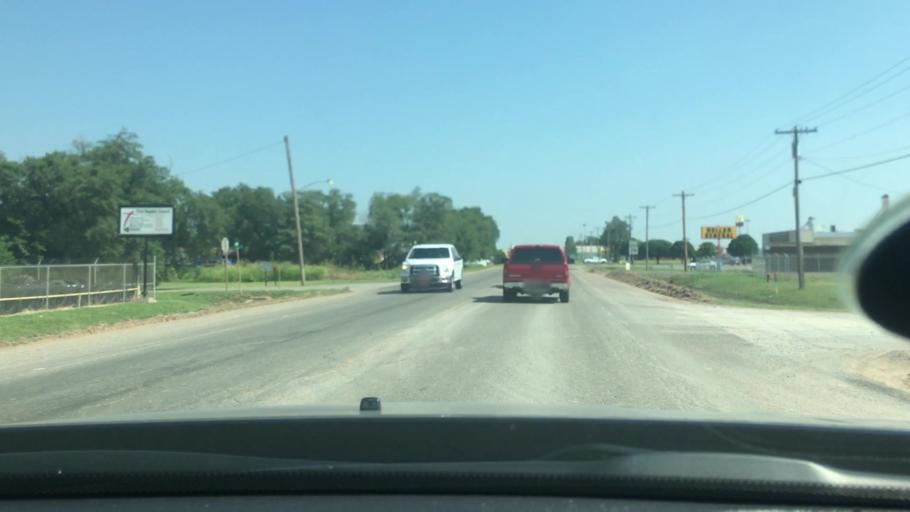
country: US
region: Oklahoma
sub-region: Garvin County
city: Lindsay
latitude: 34.8331
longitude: -97.5984
